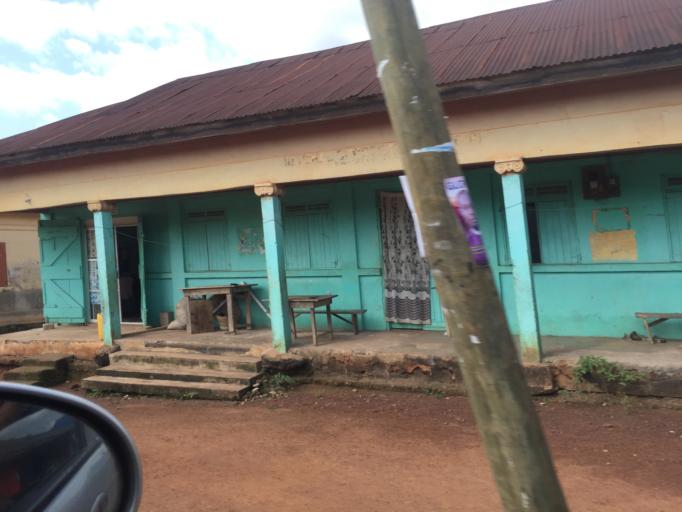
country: GH
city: Mpraeso
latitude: 6.5955
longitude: -0.7371
